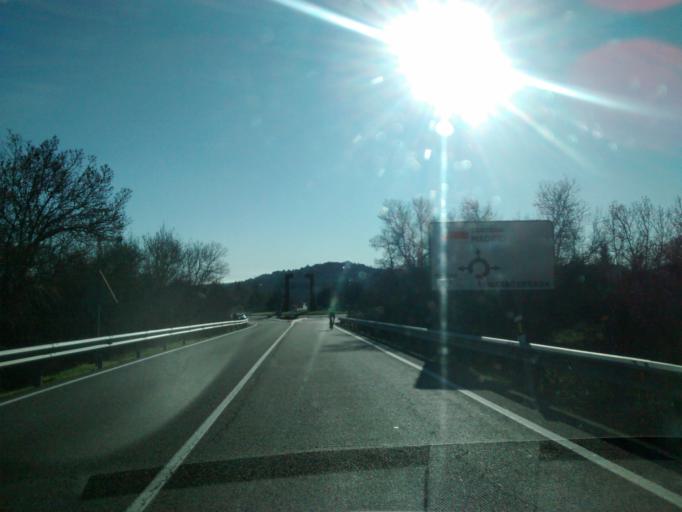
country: ES
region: Madrid
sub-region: Provincia de Madrid
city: Navacerrada
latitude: 40.7347
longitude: -4.0081
